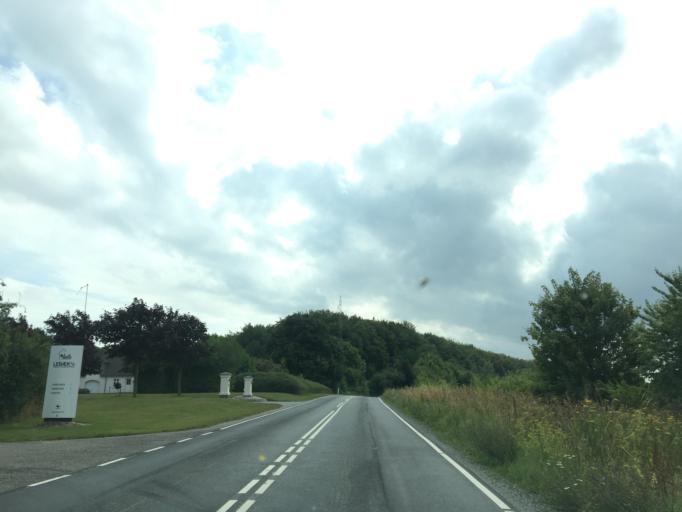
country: DK
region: South Denmark
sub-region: Assens Kommune
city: Arup
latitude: 55.4101
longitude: 10.0198
